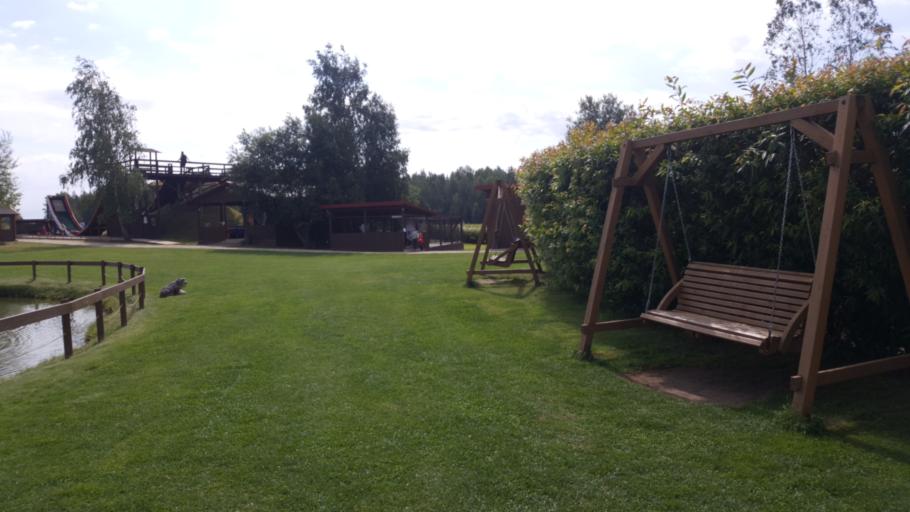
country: LT
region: Utenos apskritis
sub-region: Anyksciai
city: Anyksciai
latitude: 55.4802
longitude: 25.0809
